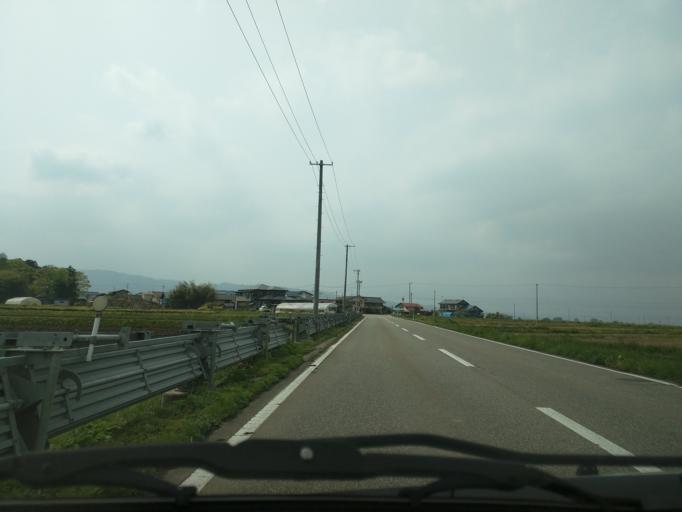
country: JP
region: Fukushima
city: Kitakata
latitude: 37.4396
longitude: 139.8592
